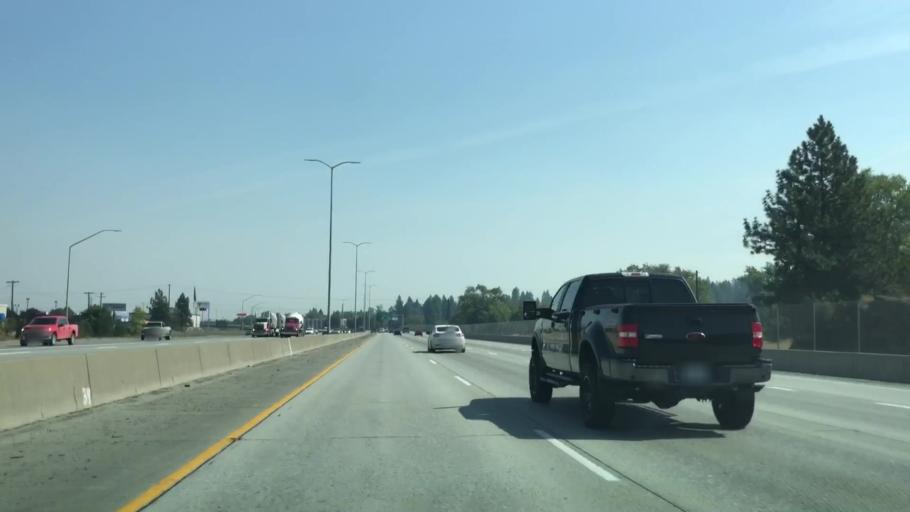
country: US
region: Washington
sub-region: Spokane County
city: Millwood
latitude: 47.6541
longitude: -117.3344
